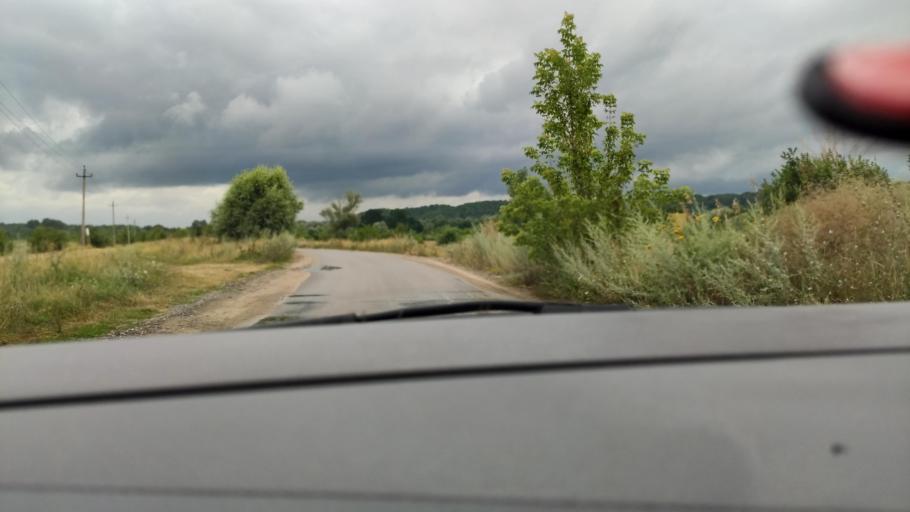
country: RU
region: Voronezj
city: Ramon'
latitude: 51.9030
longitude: 39.3513
